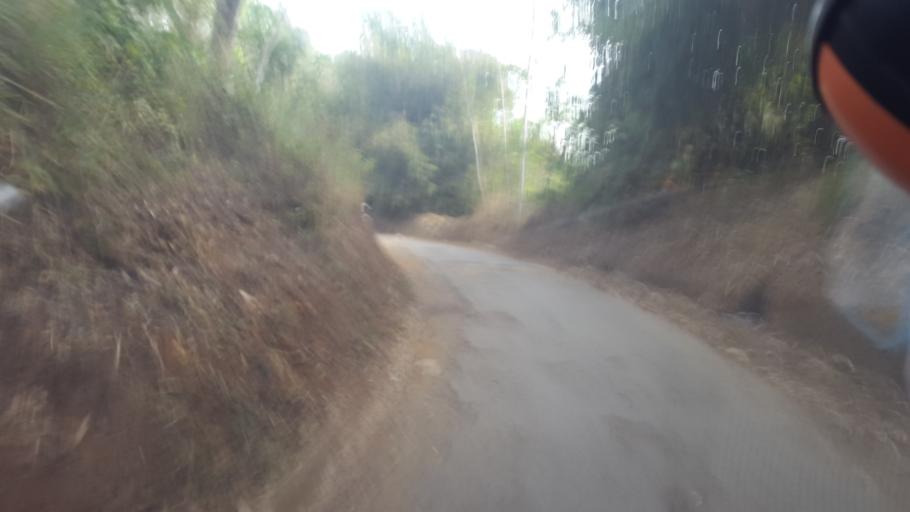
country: ID
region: West Java
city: Cilandak
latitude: -6.9451
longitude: 106.7480
